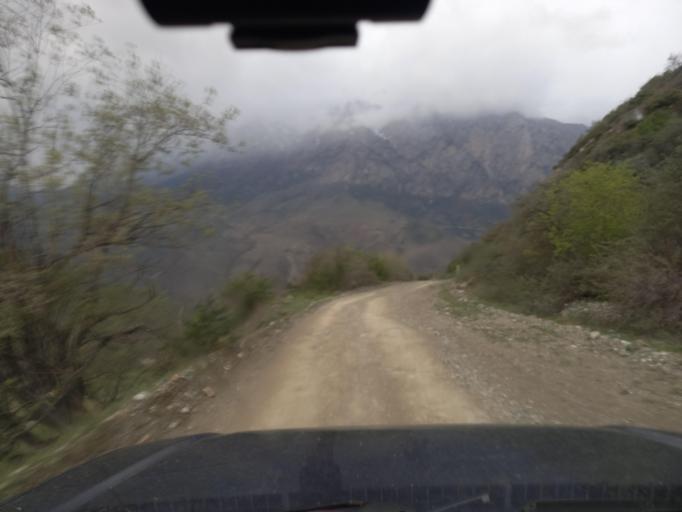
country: RU
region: North Ossetia
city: Mizur
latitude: 42.8486
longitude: 44.1638
